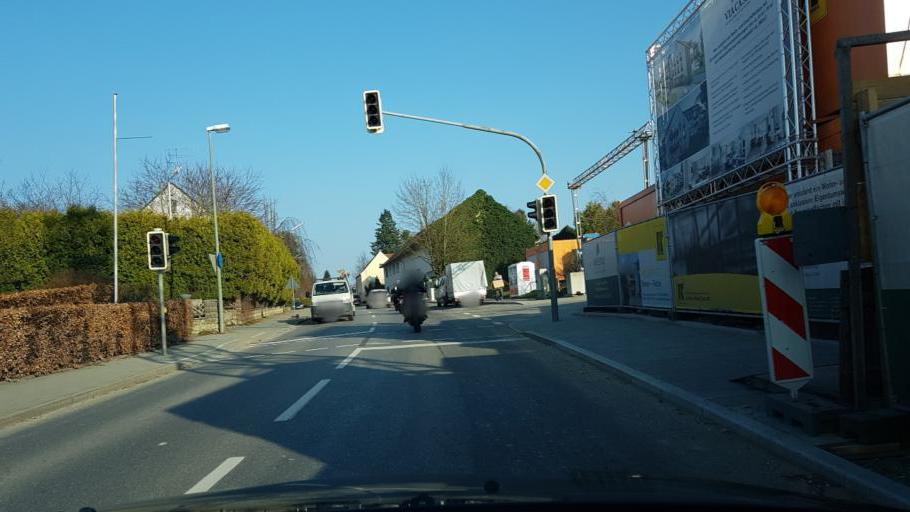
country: DE
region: Bavaria
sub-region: Upper Bavaria
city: Odelzhausen
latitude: 48.3092
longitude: 11.1951
